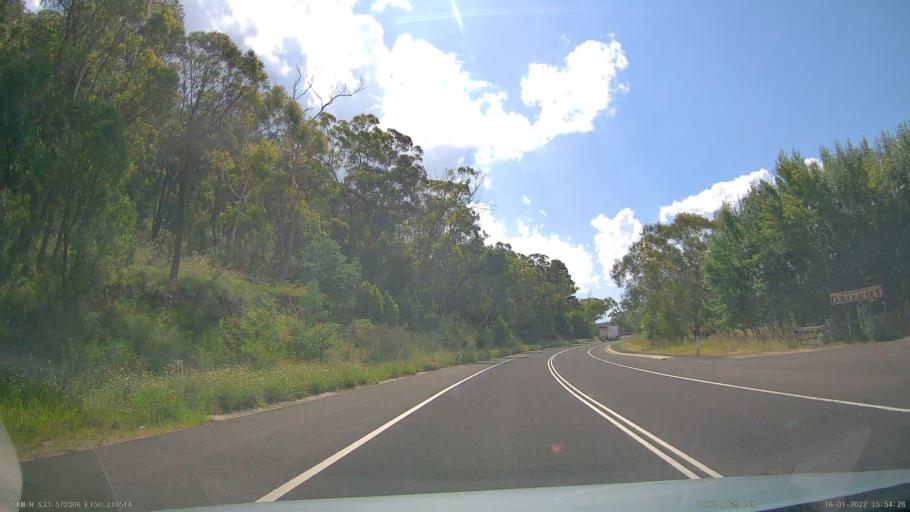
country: AU
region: New South Wales
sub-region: Blue Mountains Municipality
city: Blackheath
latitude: -33.5724
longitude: 150.2102
